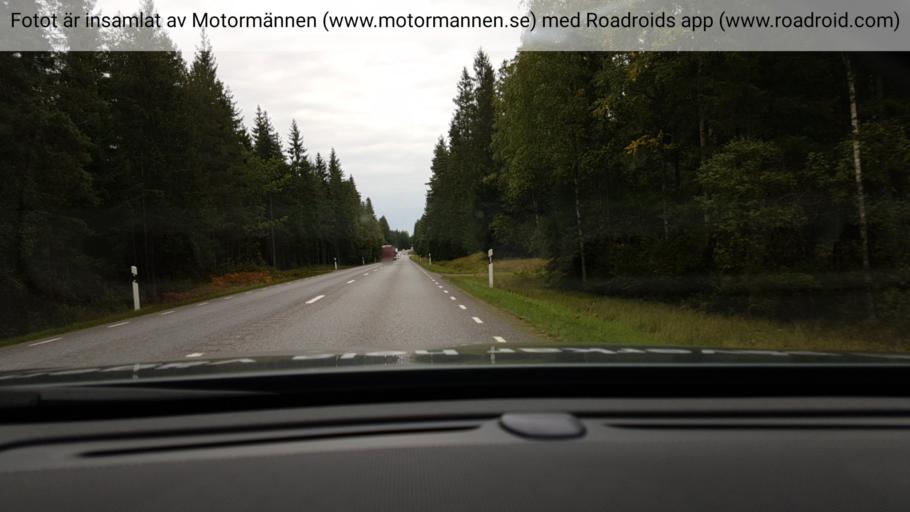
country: SE
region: Joenkoeping
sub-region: Gislaveds Kommun
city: Smalandsstenar
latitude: 57.1617
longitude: 13.4607
